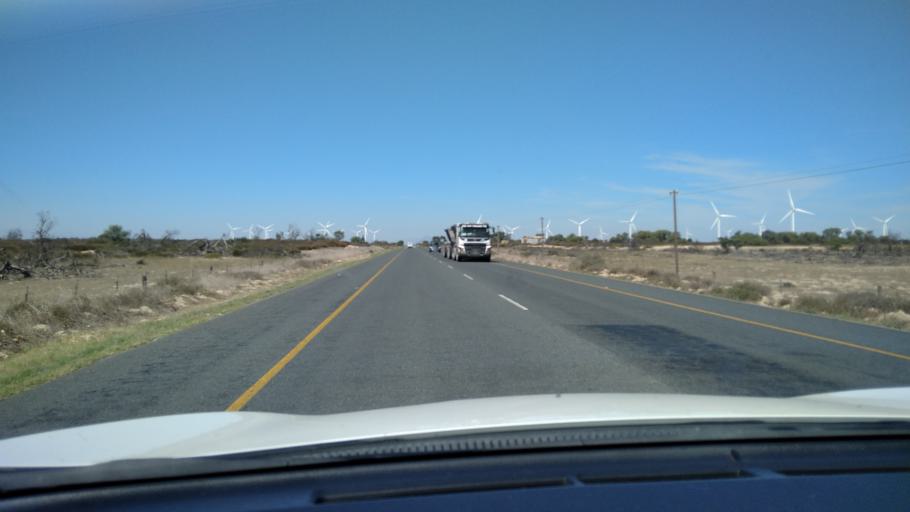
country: ZA
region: Western Cape
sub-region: West Coast District Municipality
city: Moorreesburg
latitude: -33.0679
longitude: 18.3669
